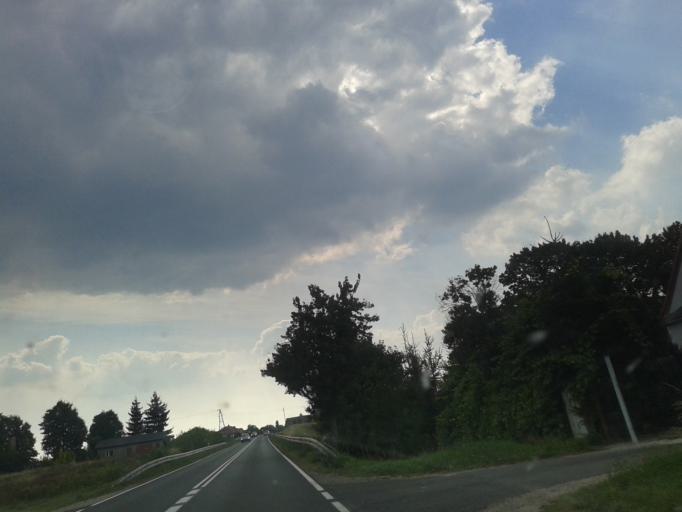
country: PL
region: West Pomeranian Voivodeship
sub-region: Powiat szczecinecki
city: Szczecinek
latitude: 53.6795
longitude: 16.6862
